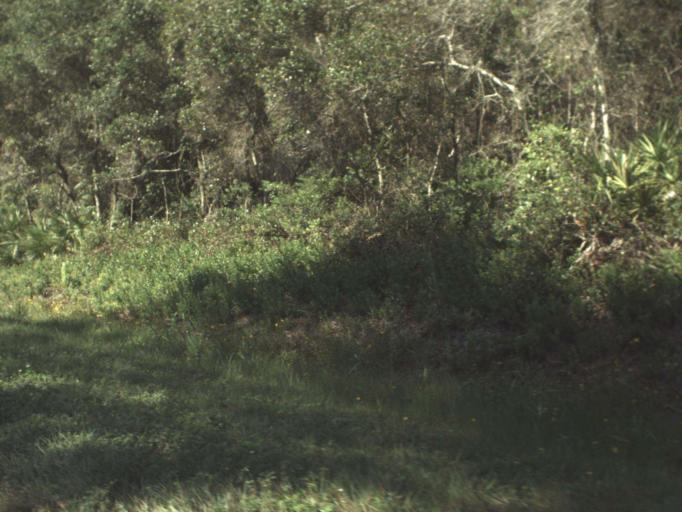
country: US
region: Florida
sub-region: Franklin County
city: Carrabelle
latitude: 29.9116
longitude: -84.5340
